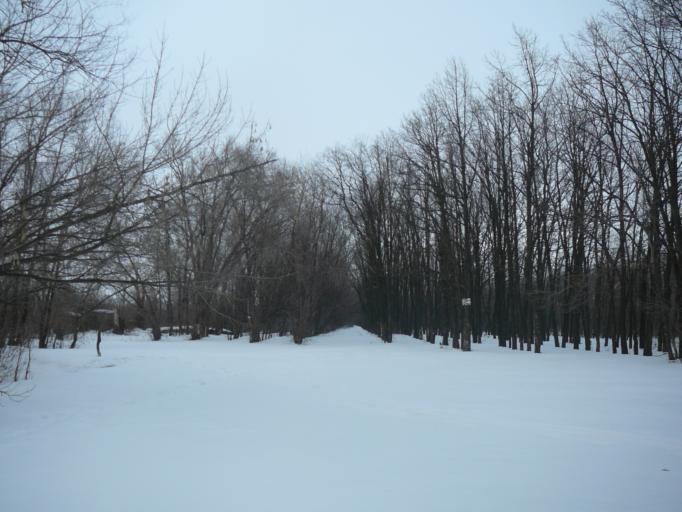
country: RU
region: Saratov
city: Engel's
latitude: 51.4603
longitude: 46.1729
